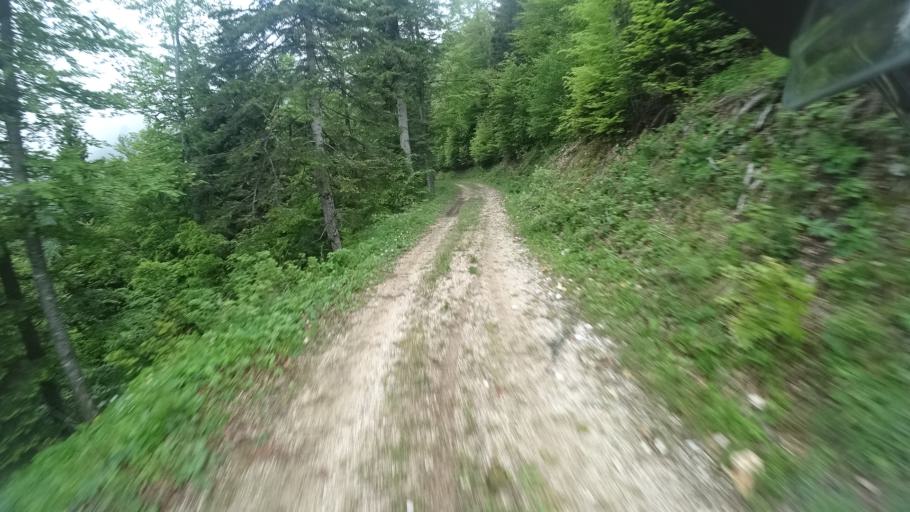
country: BA
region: Federation of Bosnia and Herzegovina
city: Bihac
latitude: 44.6124
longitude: 15.8445
